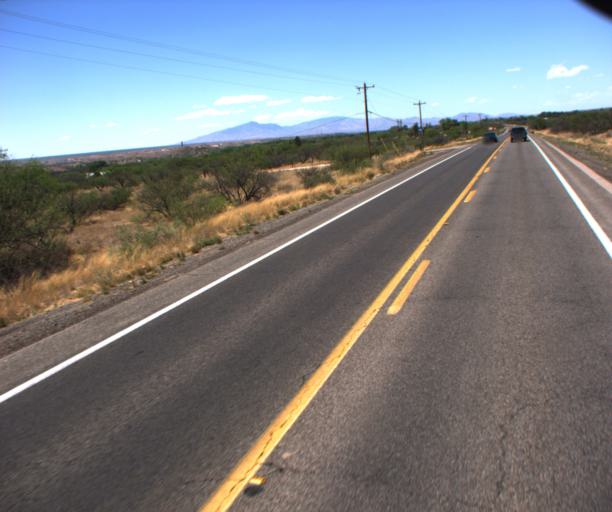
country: US
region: Arizona
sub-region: Cochise County
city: Saint David
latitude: 31.8537
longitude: -110.2006
